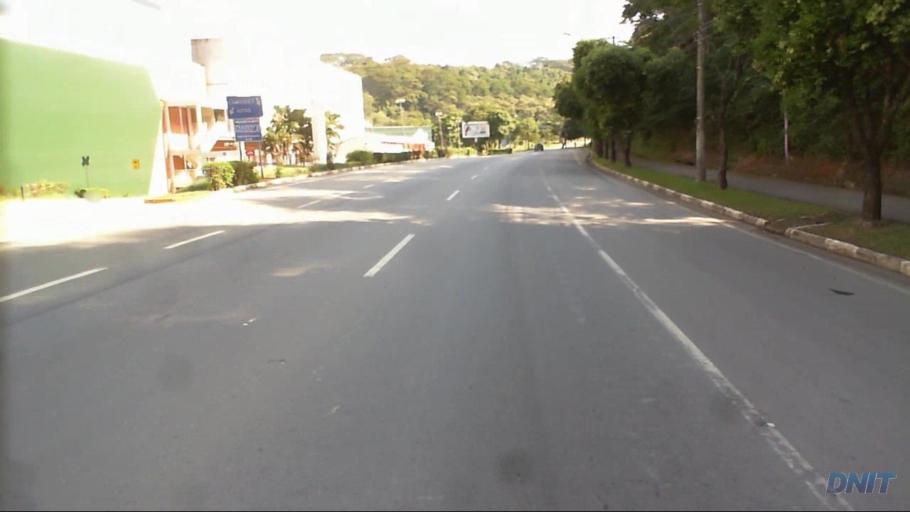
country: BR
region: Minas Gerais
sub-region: Ipatinga
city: Ipatinga
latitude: -19.4947
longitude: -42.5655
